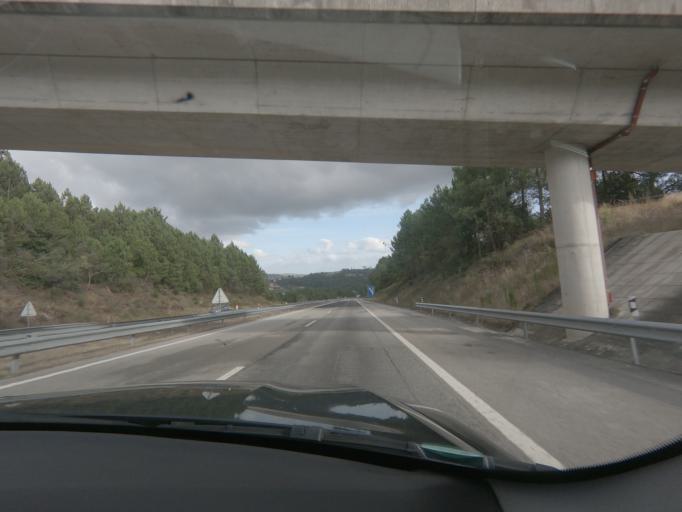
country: PT
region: Viseu
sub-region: Castro Daire
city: Castro Daire
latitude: 40.9161
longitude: -7.9124
